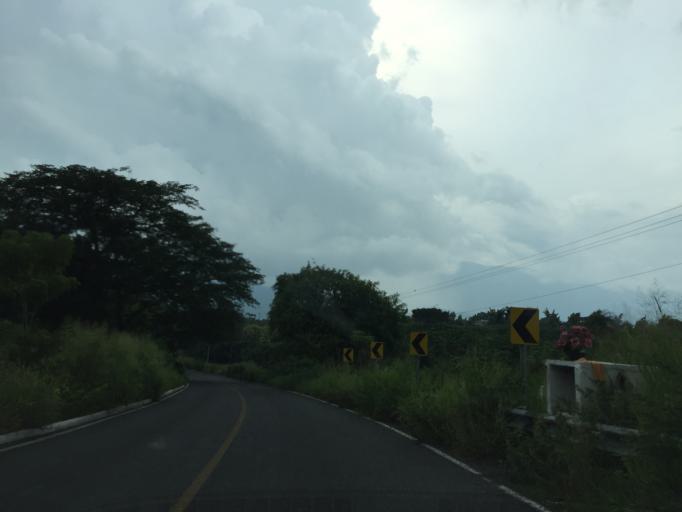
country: MX
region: Colima
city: Comala
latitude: 19.3361
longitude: -103.7713
